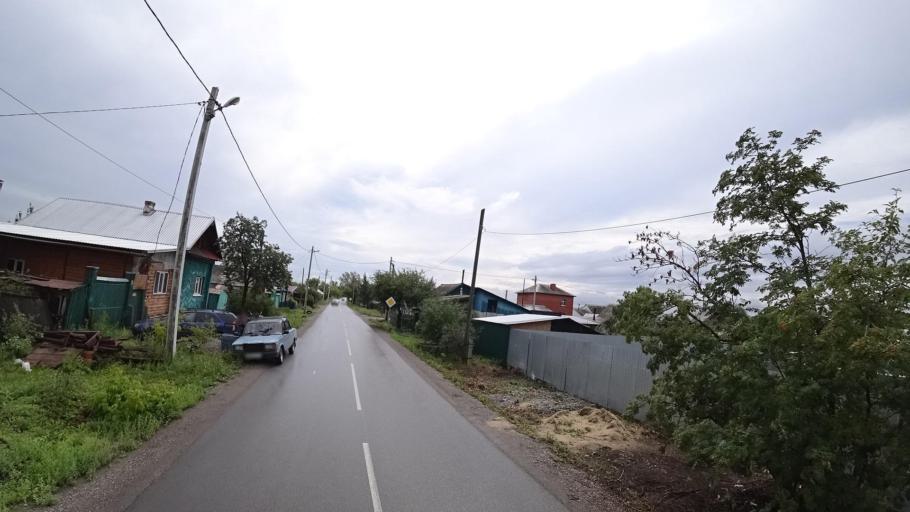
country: RU
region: Sverdlovsk
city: Kamyshlov
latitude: 56.8524
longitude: 62.7373
